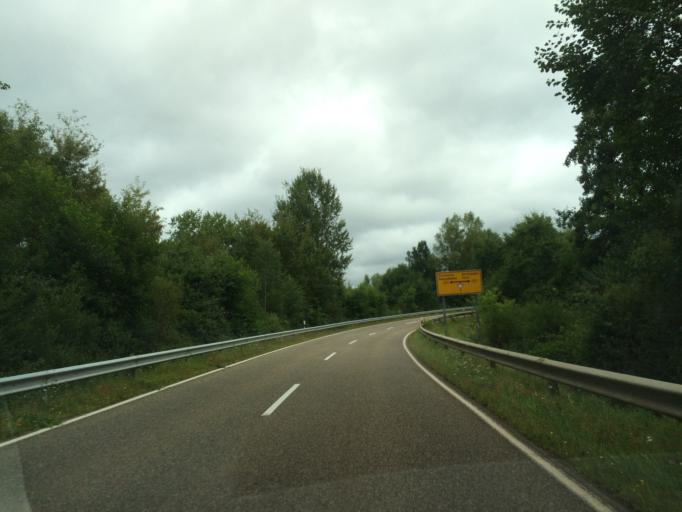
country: DE
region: Rheinland-Pfalz
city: Hinterweidenthal
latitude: 49.1767
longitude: 7.7442
